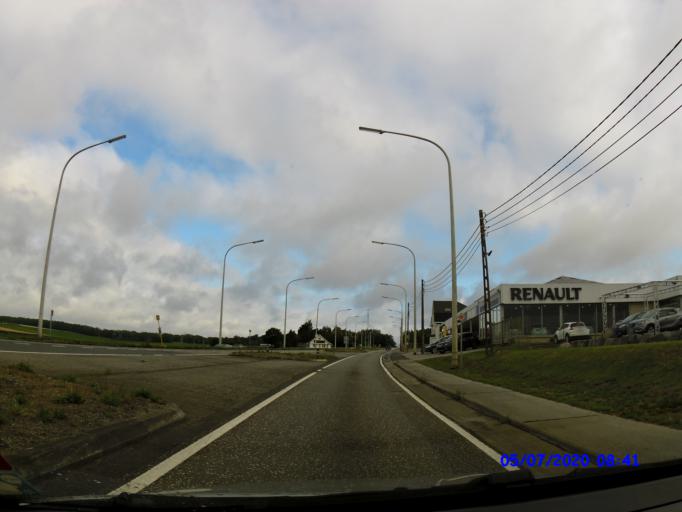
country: BE
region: Wallonia
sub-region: Province du Brabant Wallon
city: Genappe
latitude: 50.6176
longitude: 4.4443
